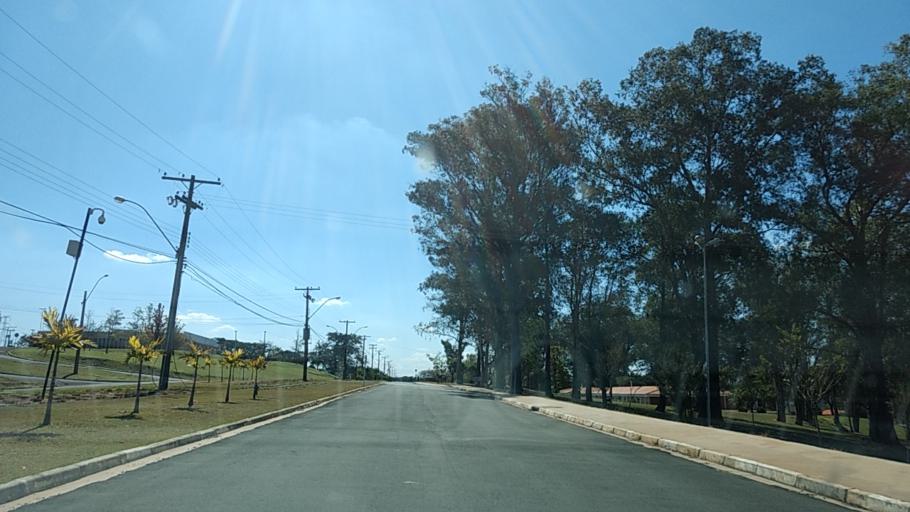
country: BR
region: Sao Paulo
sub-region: Botucatu
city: Botucatu
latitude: -22.8518
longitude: -48.4330
